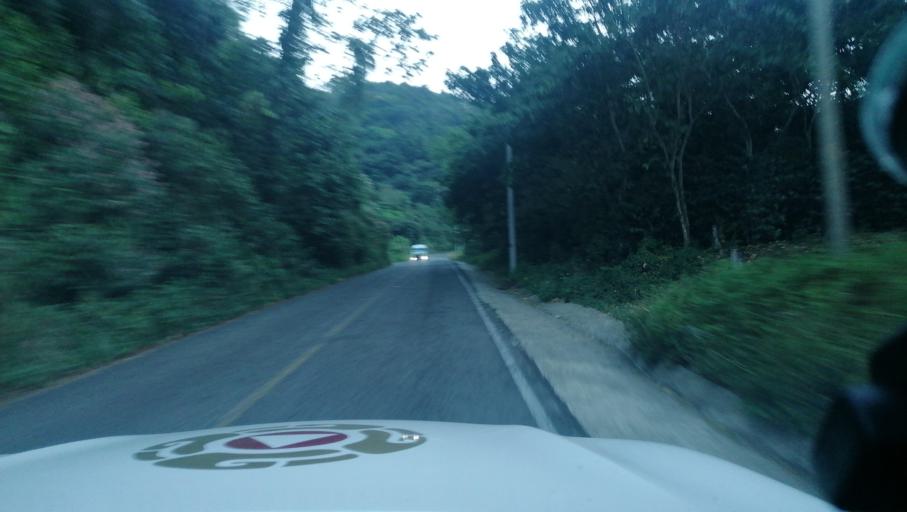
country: MX
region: Chiapas
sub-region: Cacahoatan
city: Benito Juarez
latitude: 15.0430
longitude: -92.2443
